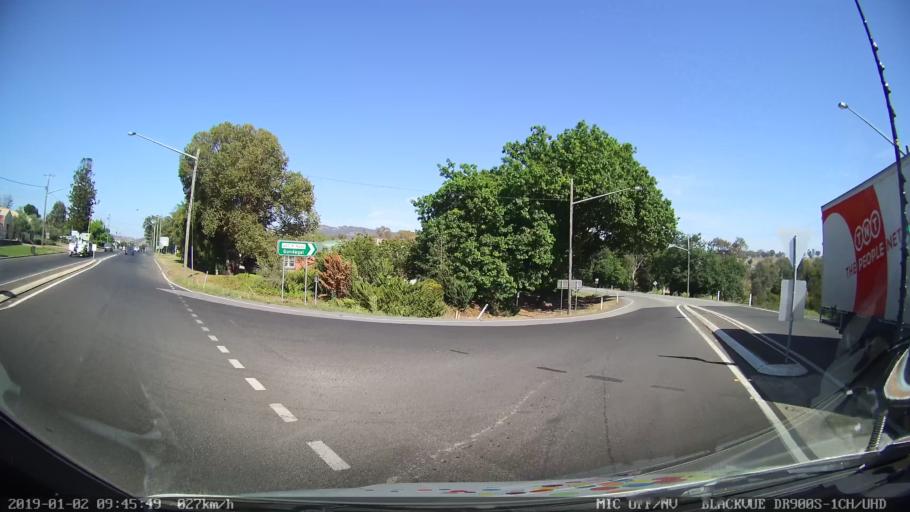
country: AU
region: New South Wales
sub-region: Tumut Shire
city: Tumut
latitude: -35.2946
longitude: 148.2160
